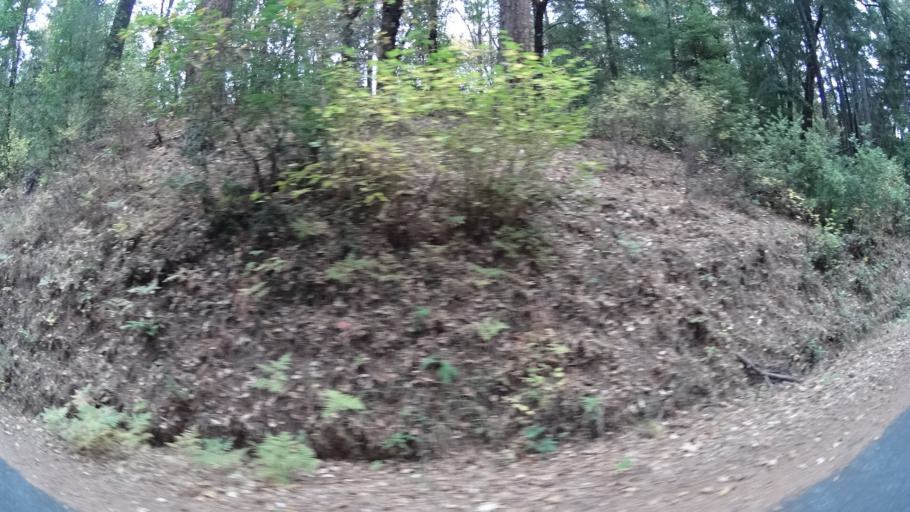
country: US
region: California
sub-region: Siskiyou County
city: Happy Camp
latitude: 41.7762
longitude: -123.3814
